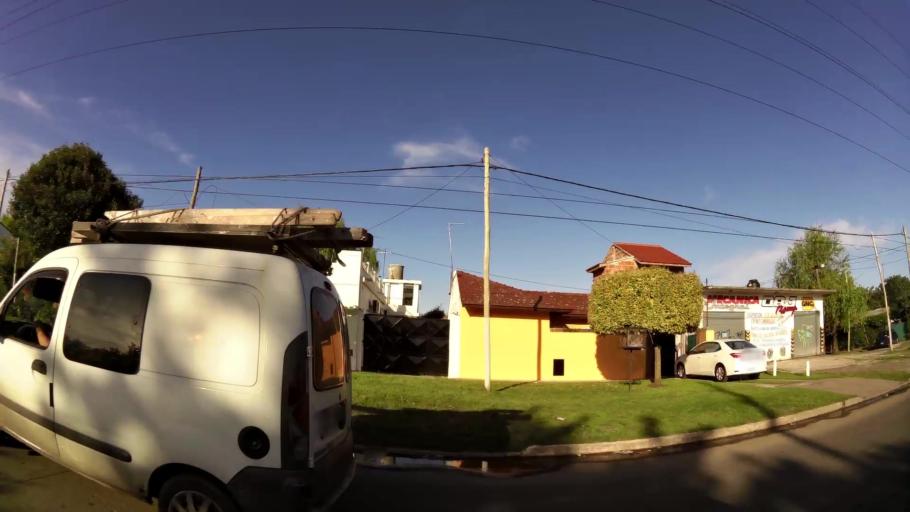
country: AR
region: Buenos Aires
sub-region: Partido de Quilmes
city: Quilmes
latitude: -34.7985
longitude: -58.2114
